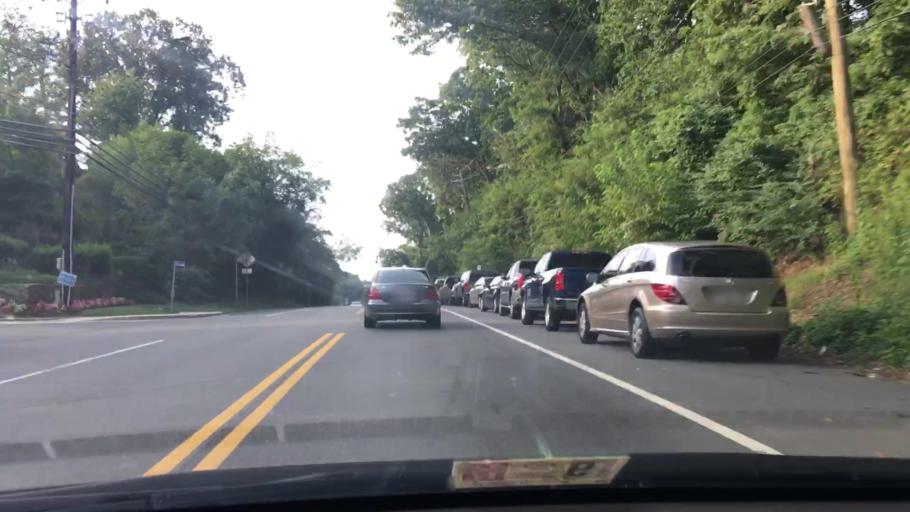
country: US
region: Maryland
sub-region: Montgomery County
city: North Bethesda
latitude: 39.0306
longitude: -77.1617
